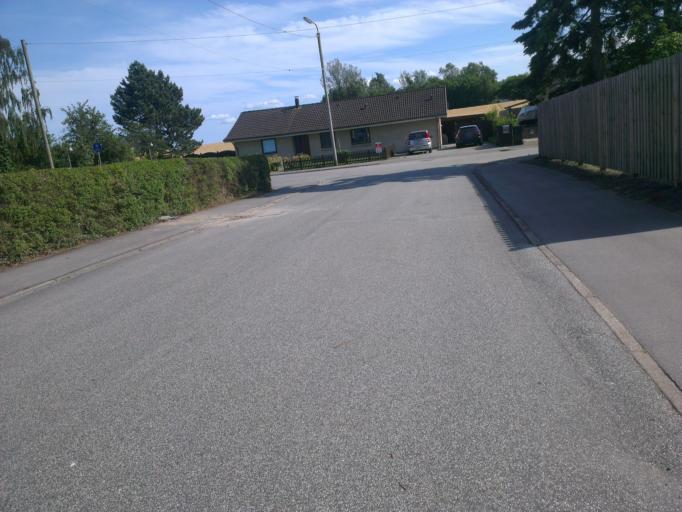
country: DK
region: Capital Region
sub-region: Frederikssund Kommune
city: Skibby
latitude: 55.7515
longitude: 11.9674
